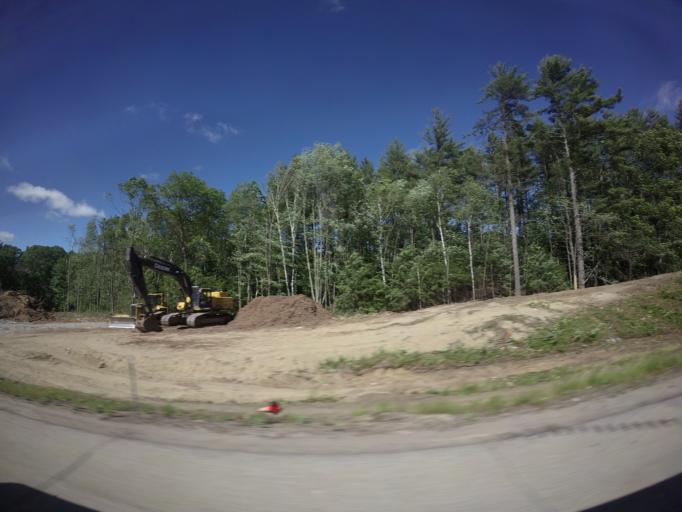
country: US
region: New Hampshire
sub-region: Rockingham County
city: Auburn
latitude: 42.9428
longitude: -71.3877
